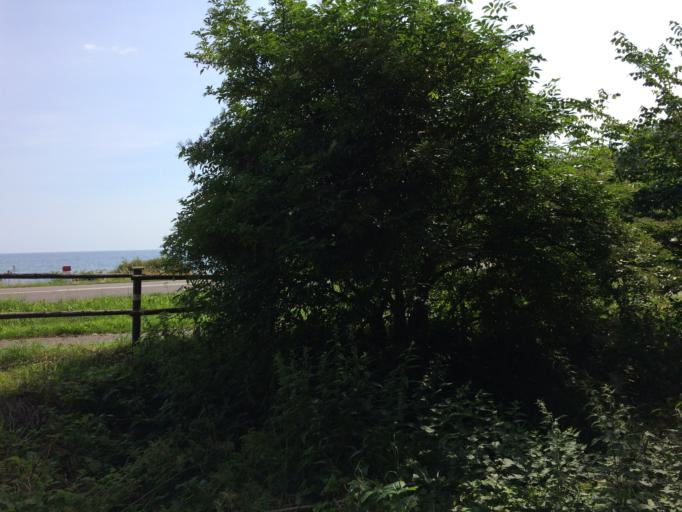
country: DK
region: Capital Region
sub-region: Bornholm Kommune
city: Akirkeby
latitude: 55.1939
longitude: 14.9880
